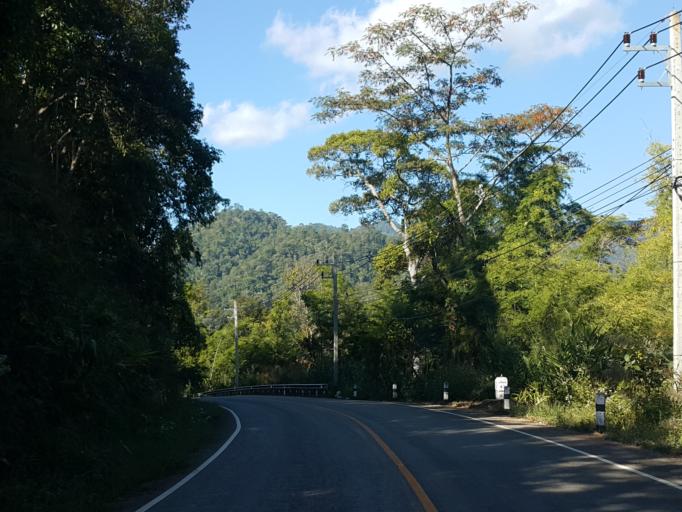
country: TH
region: Chiang Mai
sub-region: Amphoe Chiang Dao
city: Chiang Dao
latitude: 19.5254
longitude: 98.8671
